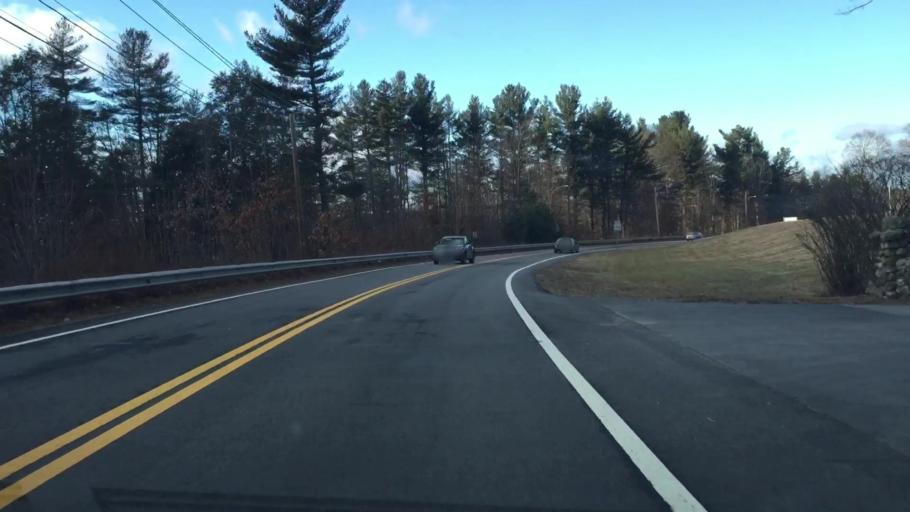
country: US
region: Massachusetts
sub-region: Worcester County
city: West Boylston
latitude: 42.3819
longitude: -71.7878
